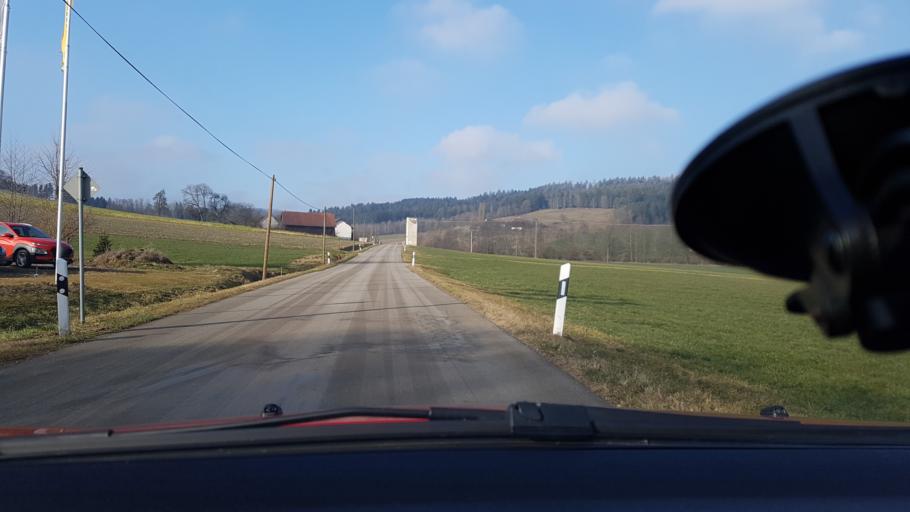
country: DE
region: Bavaria
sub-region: Lower Bavaria
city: Stubenberg
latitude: 48.3115
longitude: 13.0621
